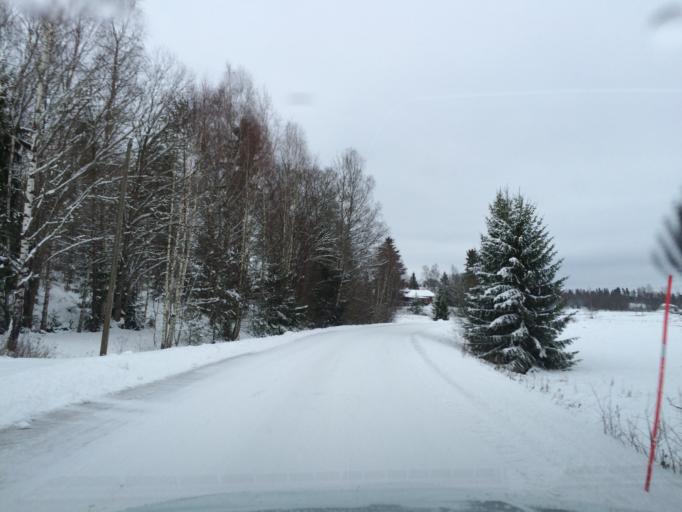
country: SE
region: Vaestmanland
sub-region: Hallstahammars Kommun
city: Kolback
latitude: 59.5874
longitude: 16.2636
